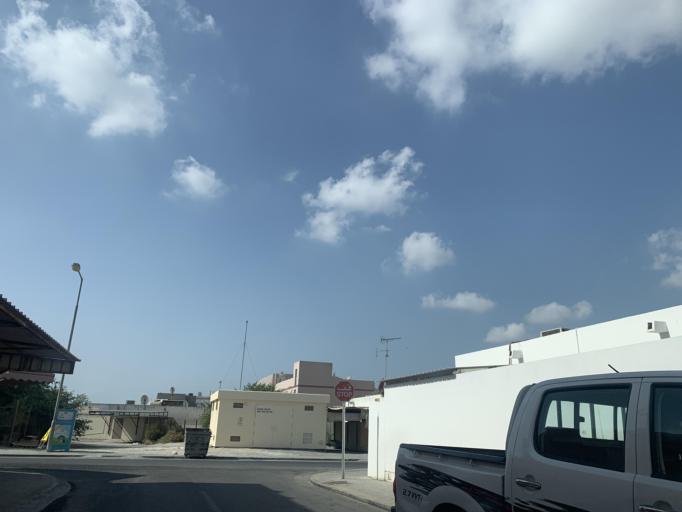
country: BH
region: Central Governorate
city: Madinat Hamad
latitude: 26.1359
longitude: 50.4995
